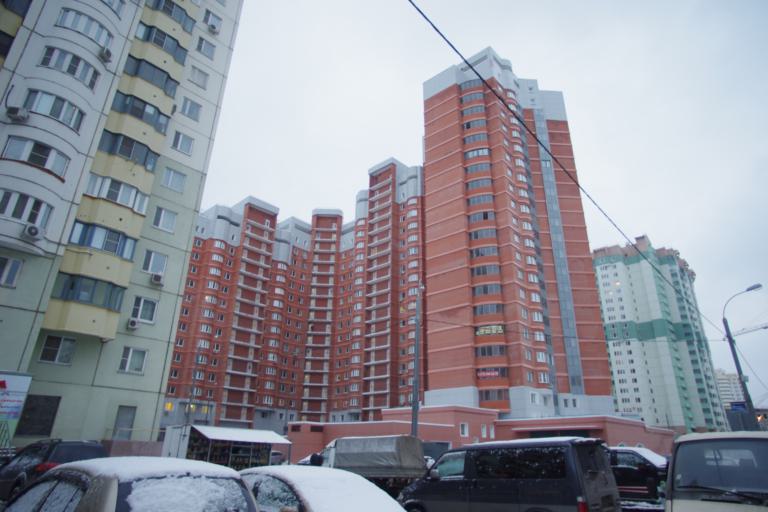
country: RU
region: Moskovskaya
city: Pavshino
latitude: 55.8221
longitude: 37.3680
